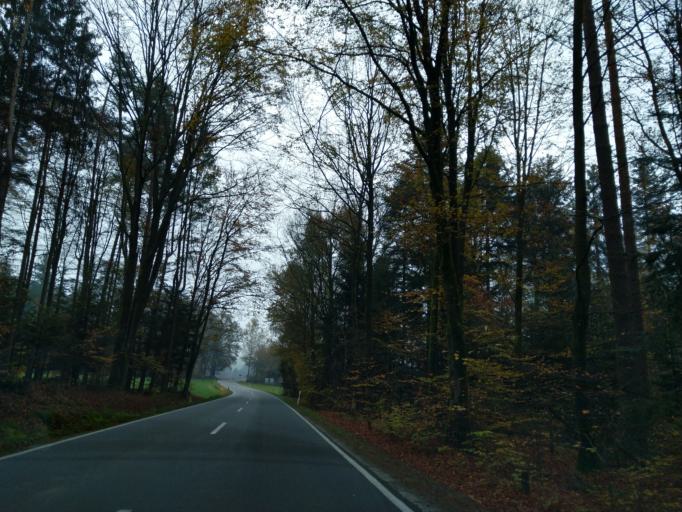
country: DE
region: Bavaria
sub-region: Lower Bavaria
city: Grattersdorf
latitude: 48.7807
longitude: 13.1689
